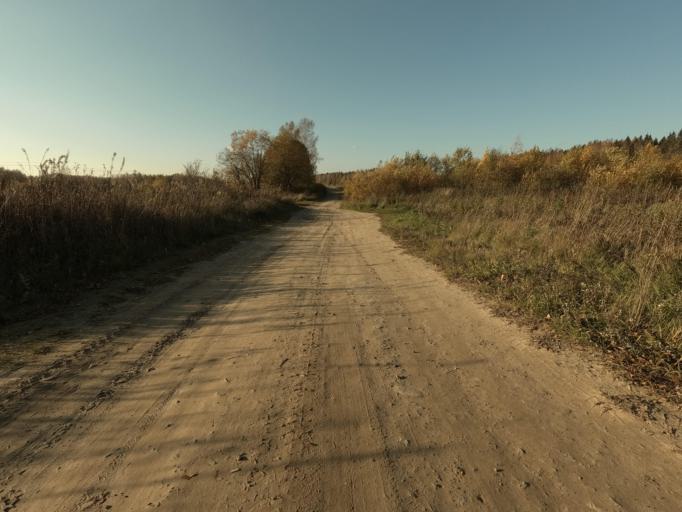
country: RU
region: Leningrad
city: Luppolovo
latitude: 60.1443
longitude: 30.2461
